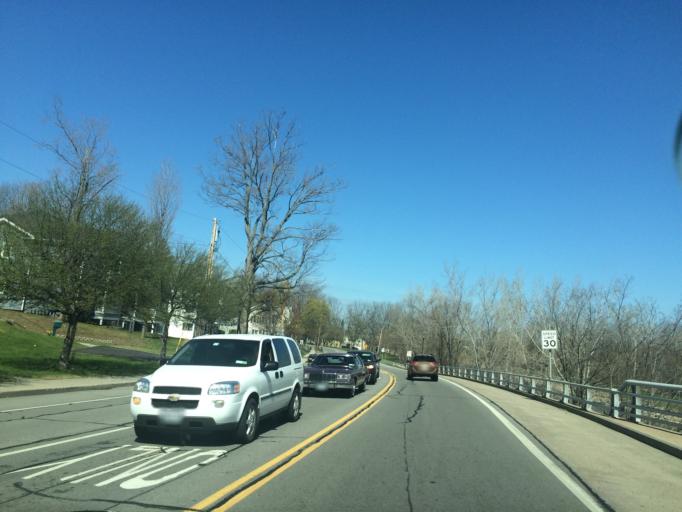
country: US
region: New York
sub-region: Monroe County
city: Fairport
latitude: 43.0970
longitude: -77.4332
